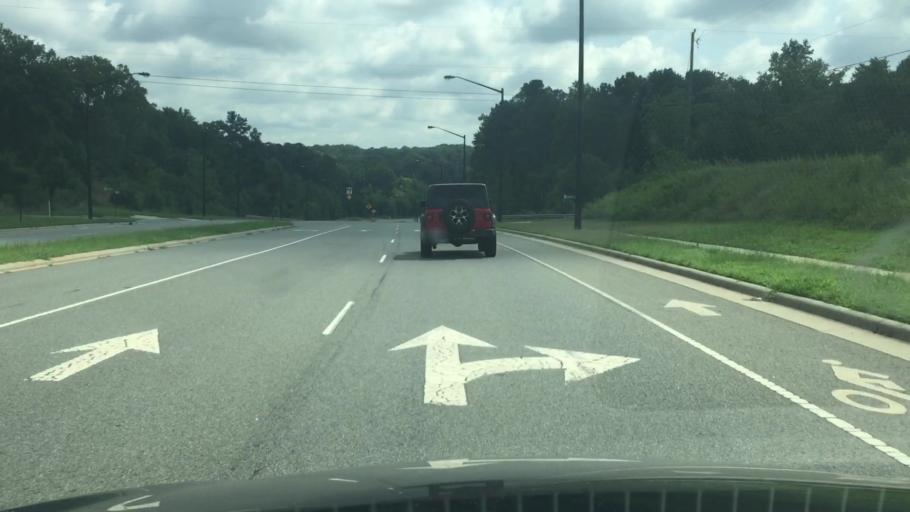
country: US
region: North Carolina
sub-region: Cabarrus County
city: Kannapolis
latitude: 35.4717
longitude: -80.6612
